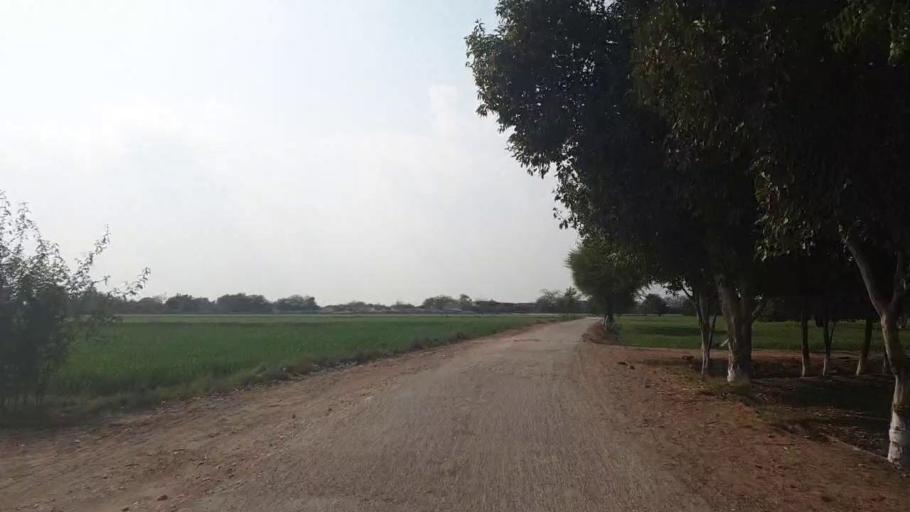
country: PK
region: Sindh
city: Hala
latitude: 25.8300
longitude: 68.4092
